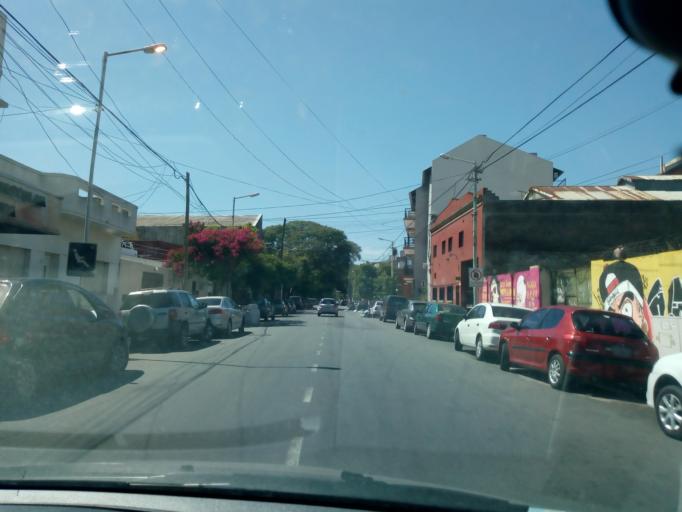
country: AR
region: Buenos Aires
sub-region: Partido de Avellaneda
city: Avellaneda
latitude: -34.6612
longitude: -58.3609
